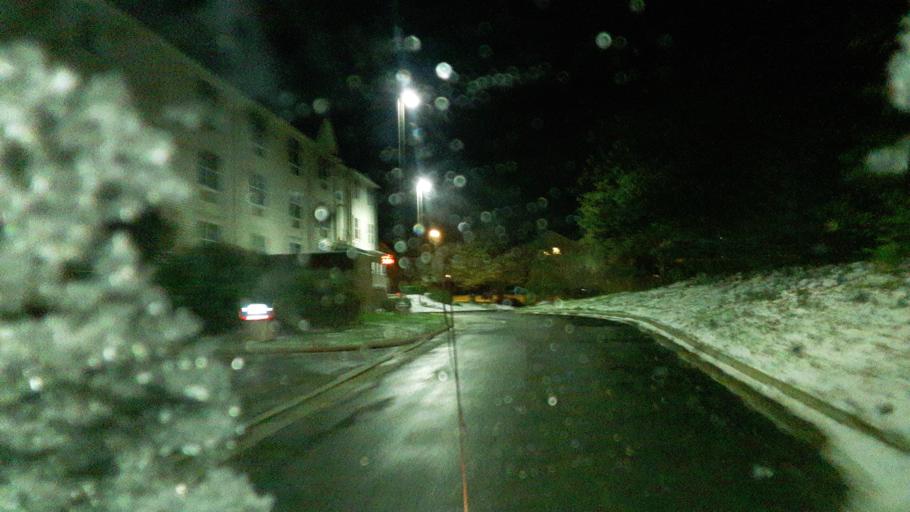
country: US
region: Ohio
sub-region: Portage County
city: Streetsboro
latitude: 41.2500
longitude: -81.3665
